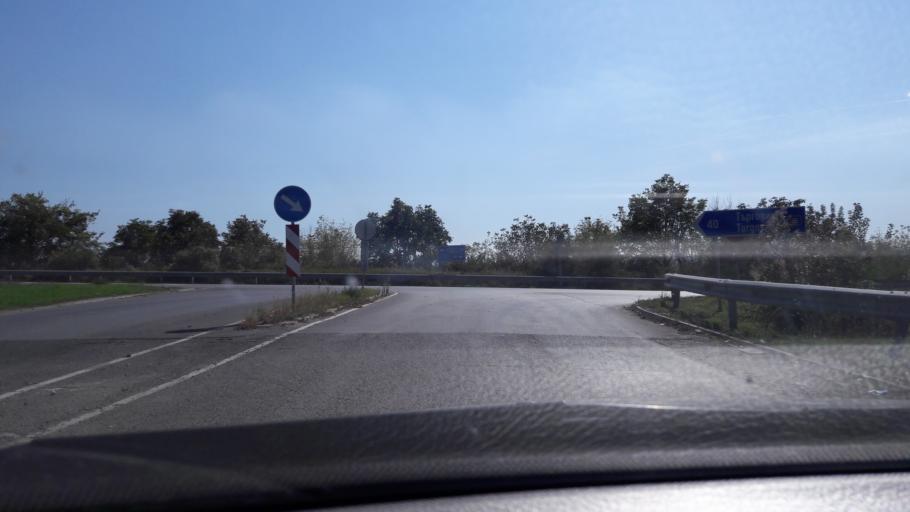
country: BG
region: Razgrad
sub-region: Obshtina Razgrad
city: Razgrad
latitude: 43.5455
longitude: 26.5133
